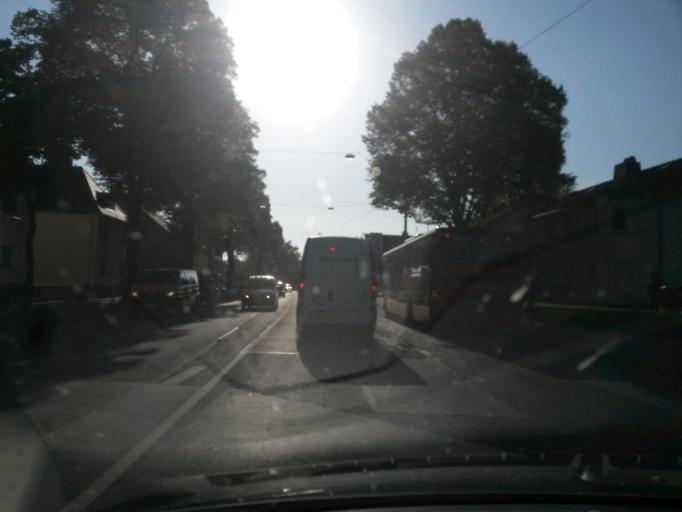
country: DE
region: North Rhine-Westphalia
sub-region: Regierungsbezirk Detmold
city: Bielefeld
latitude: 52.0122
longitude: 8.5653
